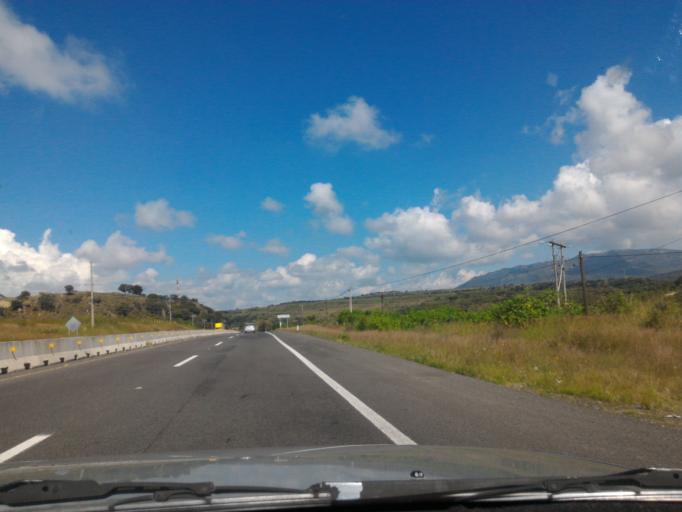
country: MX
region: Jalisco
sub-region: Tala
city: Los Ruisenores
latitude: 20.7335
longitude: -103.6225
